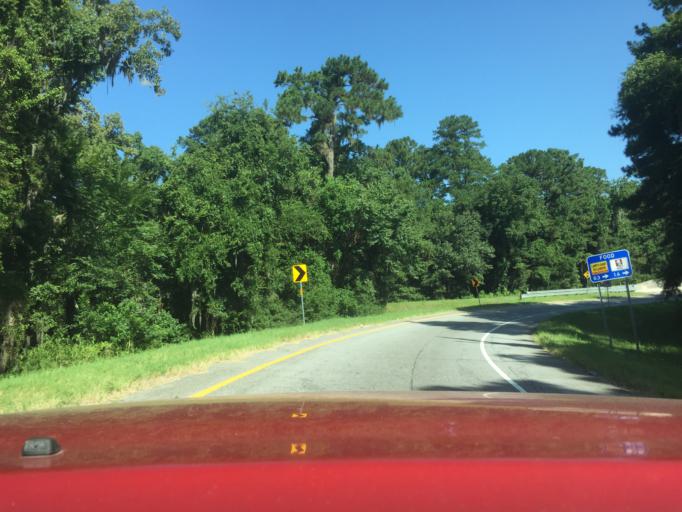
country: US
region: Georgia
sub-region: Chatham County
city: Garden City
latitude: 32.0706
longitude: -81.1626
